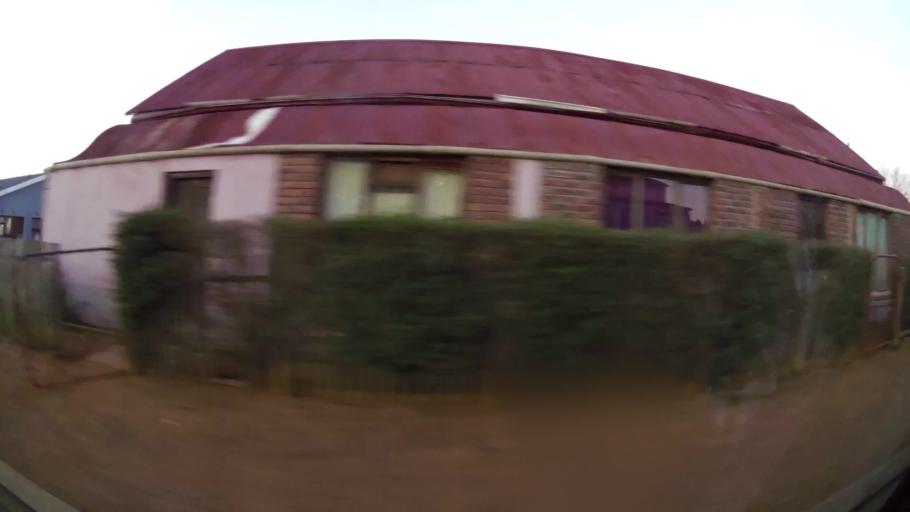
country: ZA
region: Western Cape
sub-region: Eden District Municipality
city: Riversdale
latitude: -34.0983
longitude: 21.2662
